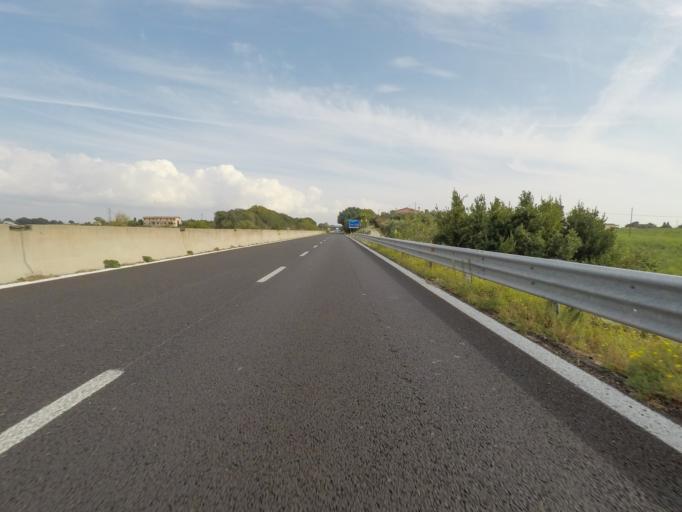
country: IT
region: Latium
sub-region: Provincia di Viterbo
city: Pescia Romana
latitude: 42.3969
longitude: 11.5187
